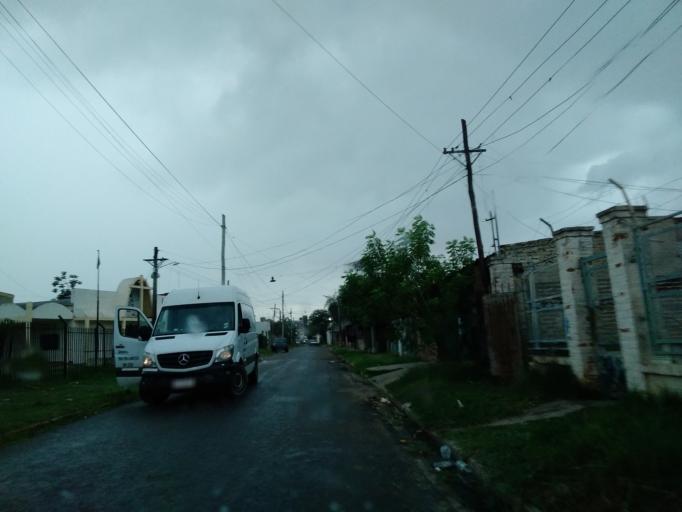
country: AR
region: Corrientes
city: Corrientes
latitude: -27.4888
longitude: -58.8249
